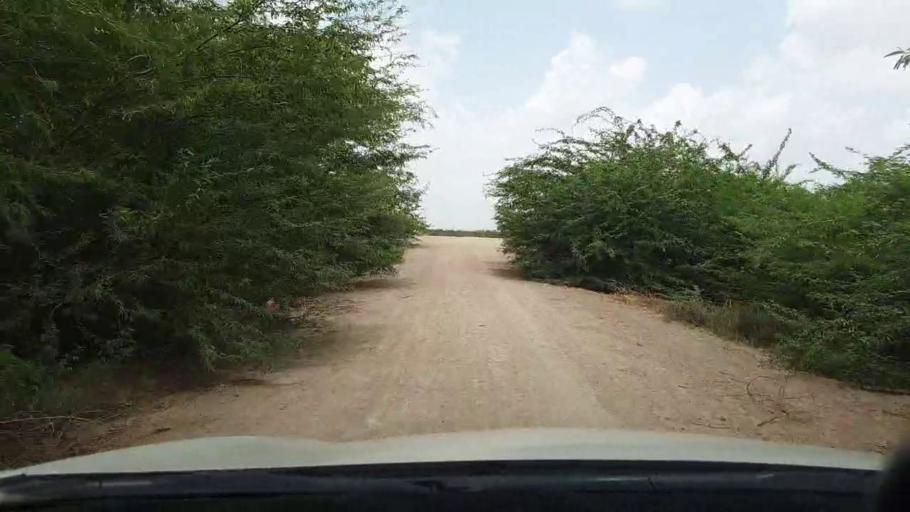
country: PK
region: Sindh
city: Kadhan
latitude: 24.3601
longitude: 68.9444
